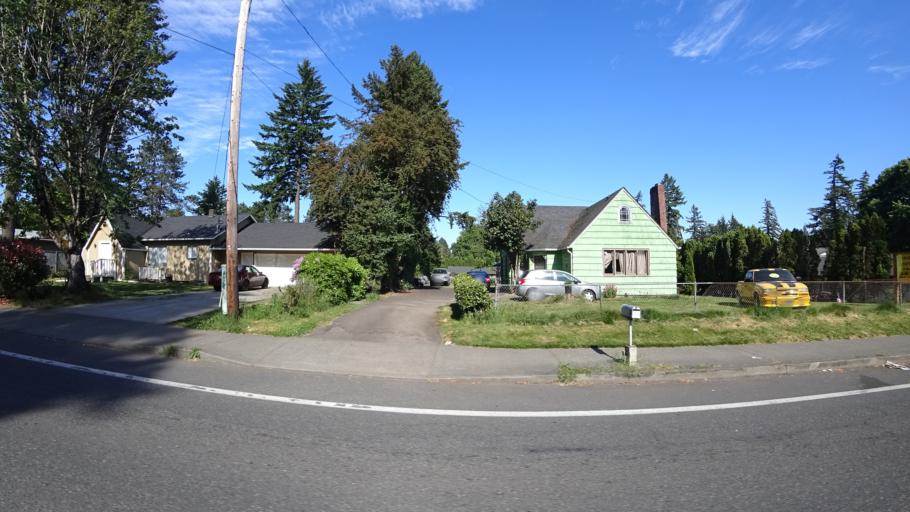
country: US
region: Oregon
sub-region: Multnomah County
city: Fairview
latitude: 45.5236
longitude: -122.4964
